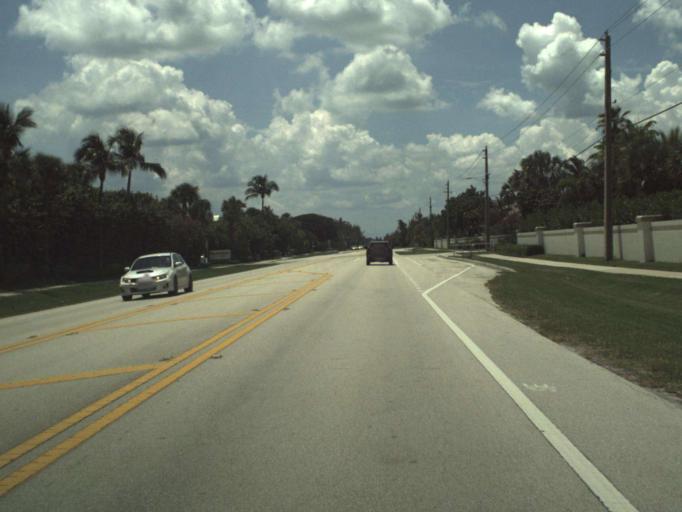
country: US
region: Florida
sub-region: Martin County
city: Sewall's Point
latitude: 27.2325
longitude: -80.1853
